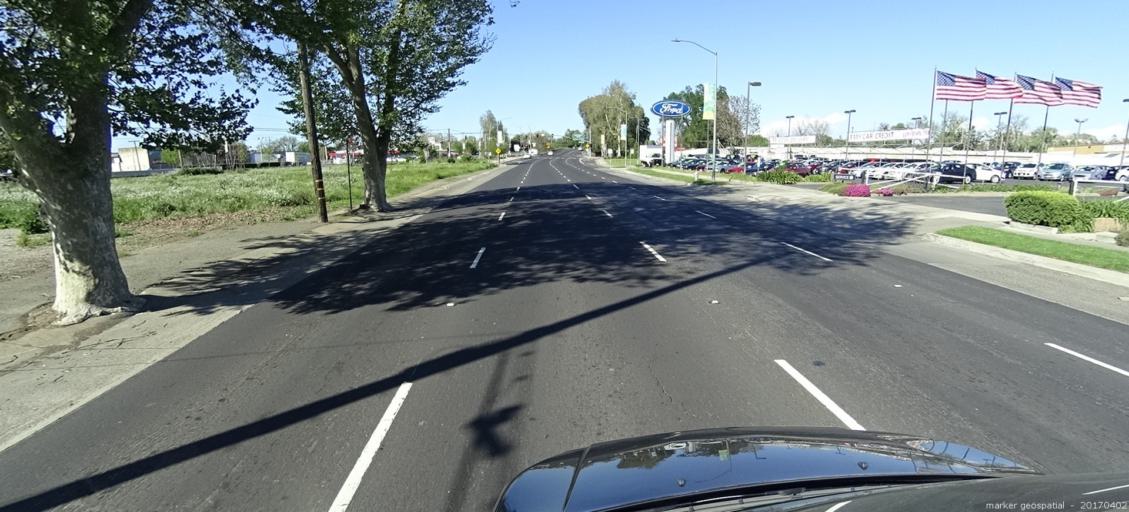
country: US
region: California
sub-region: Sacramento County
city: Sacramento
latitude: 38.5925
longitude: -121.4790
